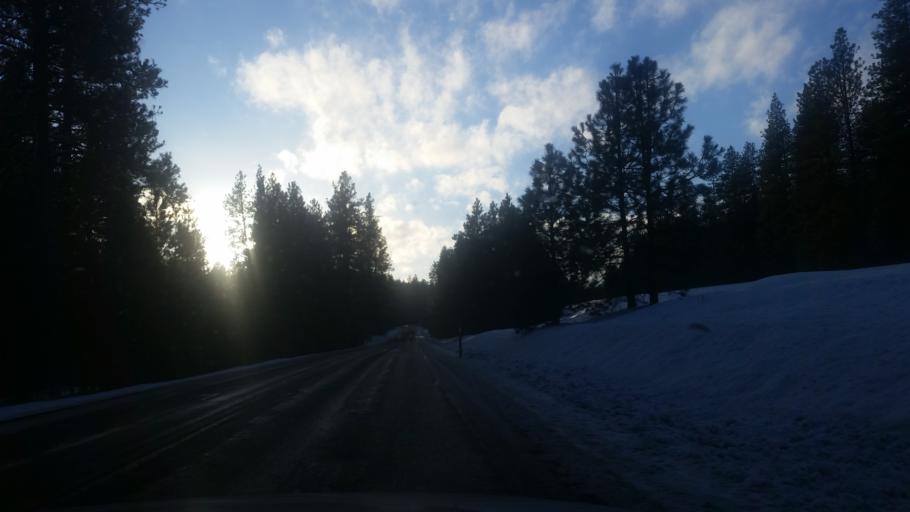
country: US
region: Washington
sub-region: Spokane County
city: Spokane
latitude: 47.5739
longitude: -117.4692
